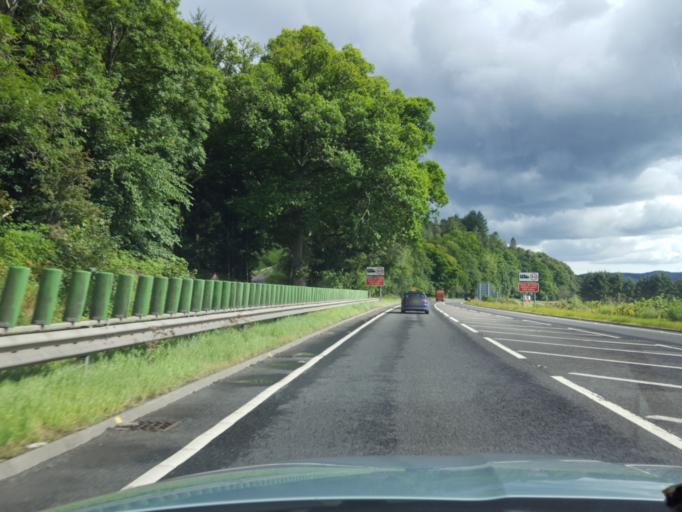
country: GB
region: Scotland
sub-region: Perth and Kinross
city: Pitlochry
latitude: 56.6451
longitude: -3.6570
